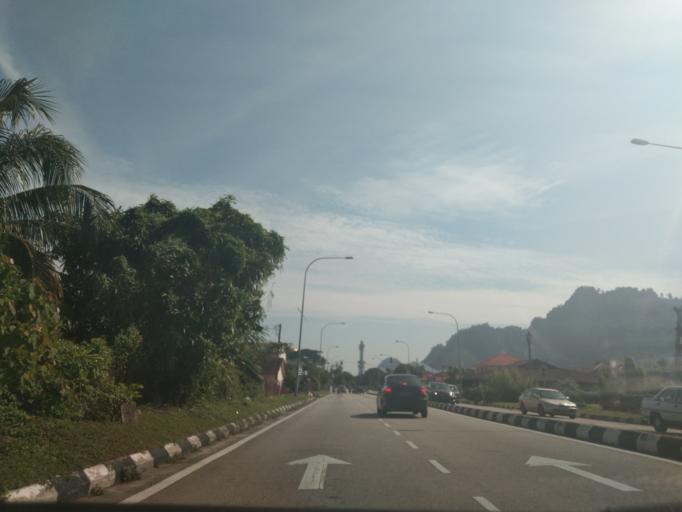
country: MY
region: Perak
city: Ipoh
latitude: 4.5856
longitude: 101.1273
